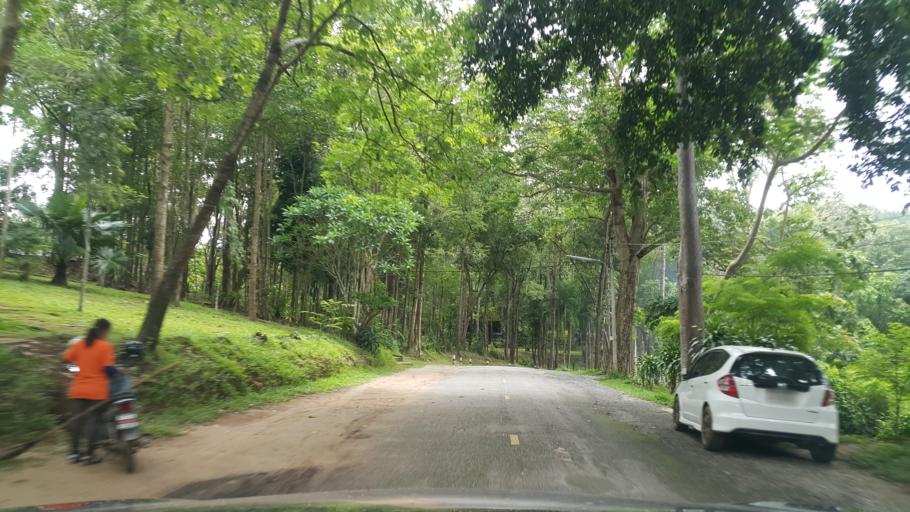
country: TH
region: Phitsanulok
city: Chat Trakan
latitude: 17.3014
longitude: 100.6776
